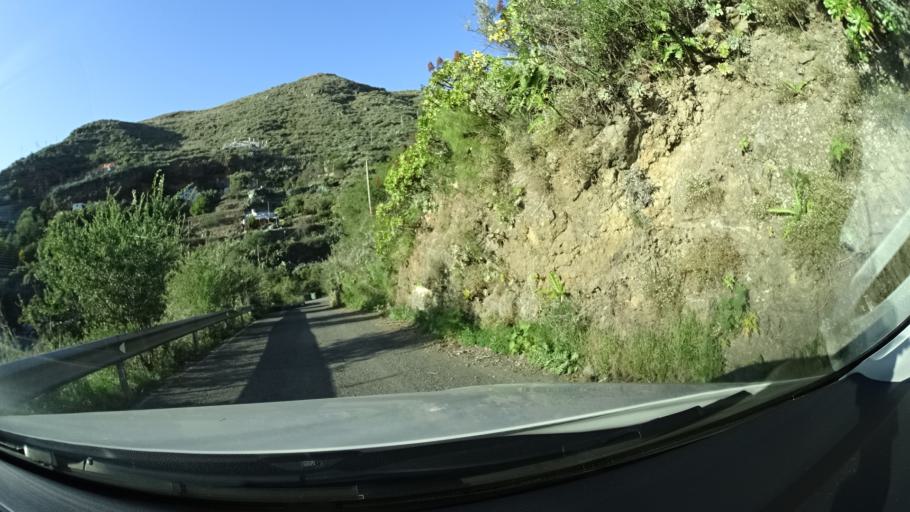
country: ES
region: Canary Islands
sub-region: Provincia de Las Palmas
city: Artenara
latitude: 28.0454
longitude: -15.6573
